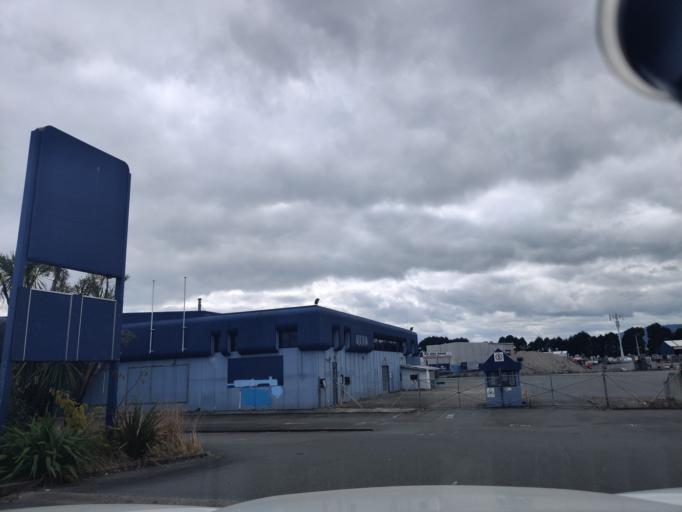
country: NZ
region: Wellington
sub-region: Kapiti Coast District
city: Paraparaumu
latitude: -40.9043
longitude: 174.9959
